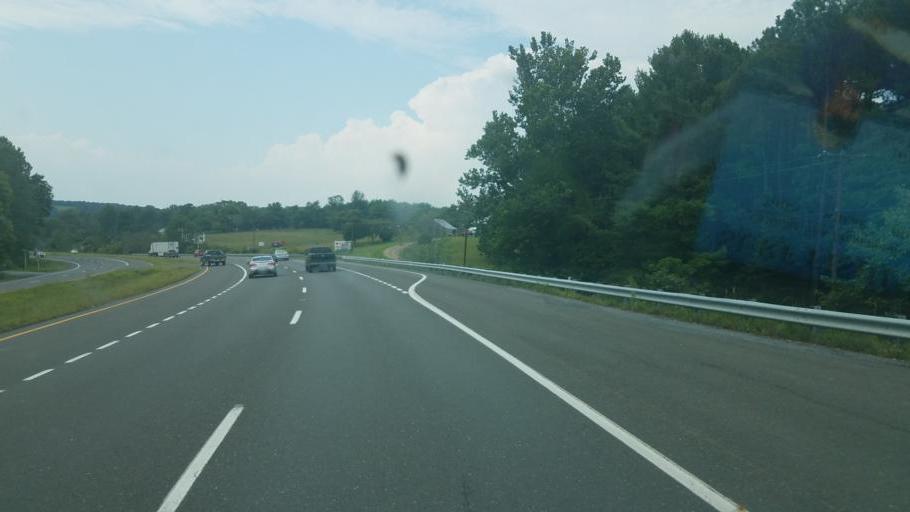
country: US
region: Virginia
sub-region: City of Winchester
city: Winchester
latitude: 39.2473
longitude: -78.2040
